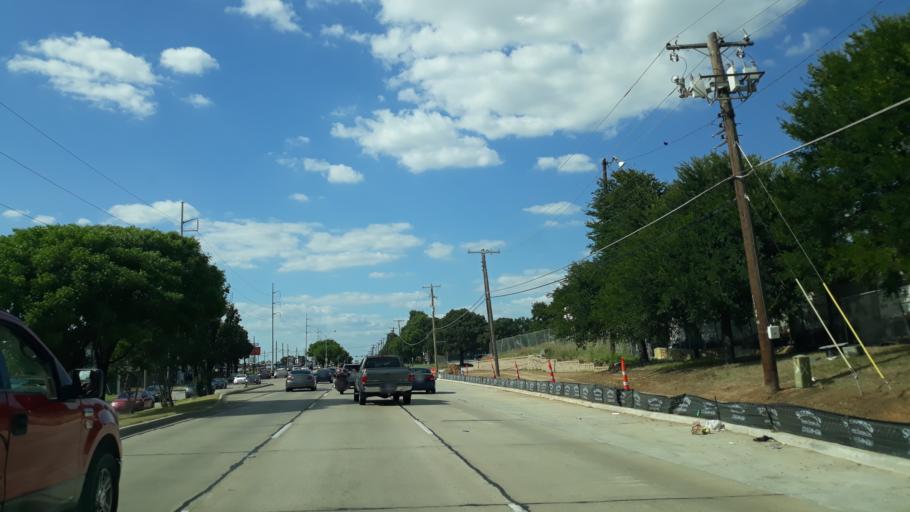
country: US
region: Texas
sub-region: Dallas County
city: Irving
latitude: 32.8177
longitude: -96.9937
